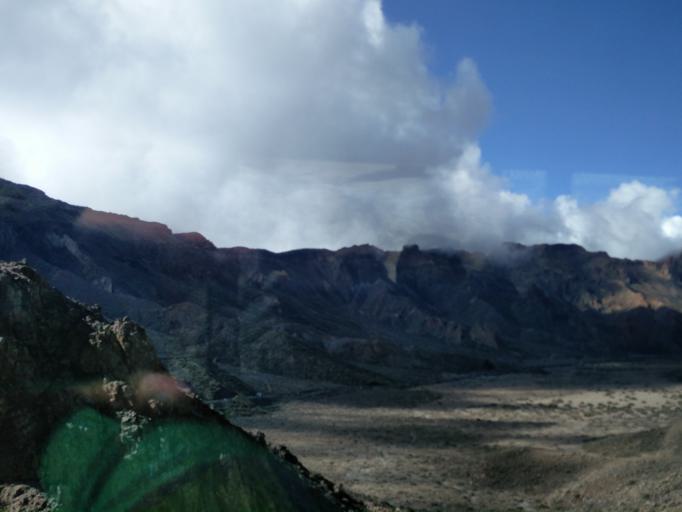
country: ES
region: Canary Islands
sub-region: Provincia de Santa Cruz de Tenerife
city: Vilaflor
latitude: 28.2176
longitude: -16.6268
